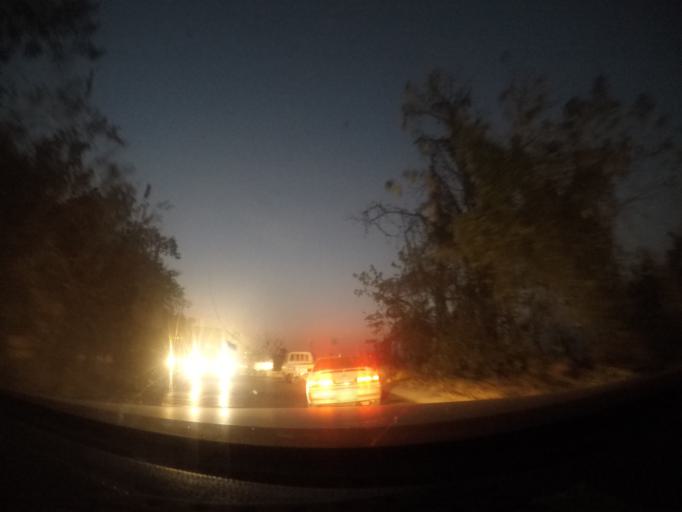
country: MM
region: Mandalay
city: Yamethin
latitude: 20.7011
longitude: 96.5175
